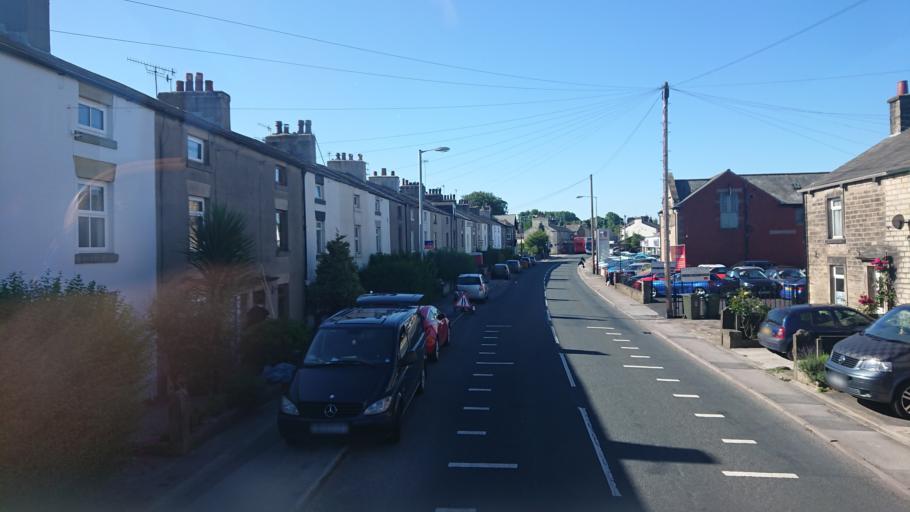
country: GB
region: England
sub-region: Lancashire
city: Galgate
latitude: 53.9936
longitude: -2.7889
